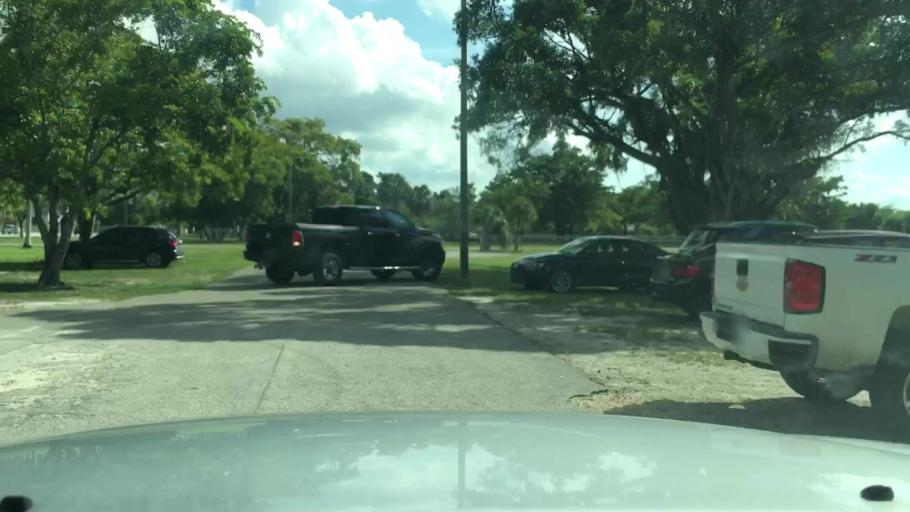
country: US
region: Florida
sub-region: Miami-Dade County
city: University Park
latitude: 25.7484
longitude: -80.3765
